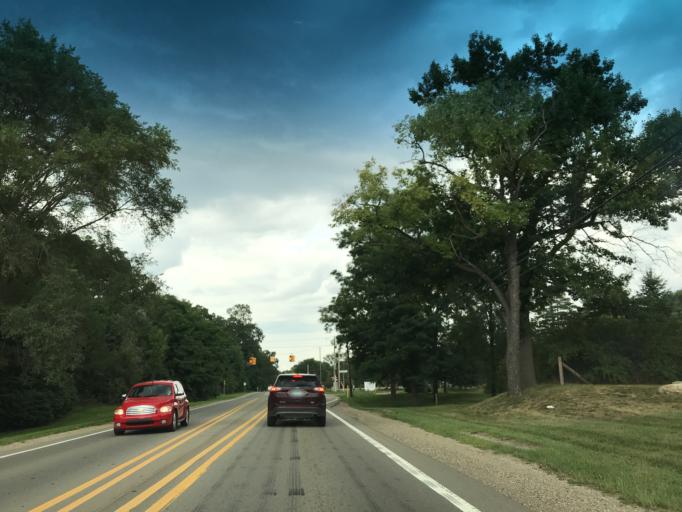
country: US
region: Michigan
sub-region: Oakland County
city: Milford
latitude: 42.5550
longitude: -83.6181
